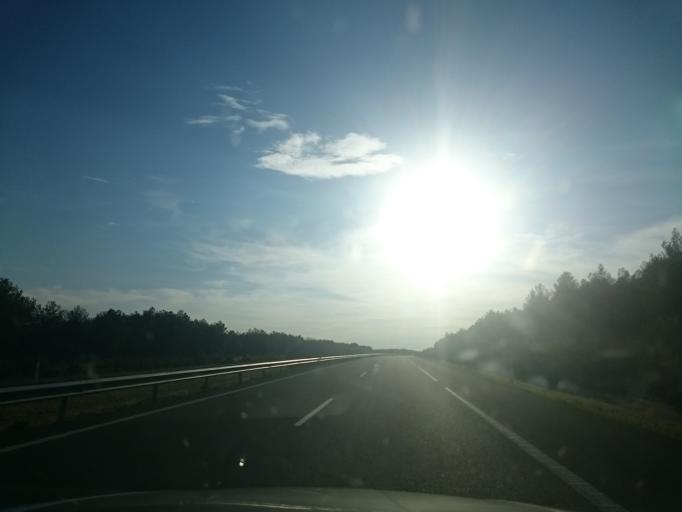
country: ES
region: Castille and Leon
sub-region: Provincia de Palencia
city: Ledigos
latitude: 42.3592
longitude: -4.8310
